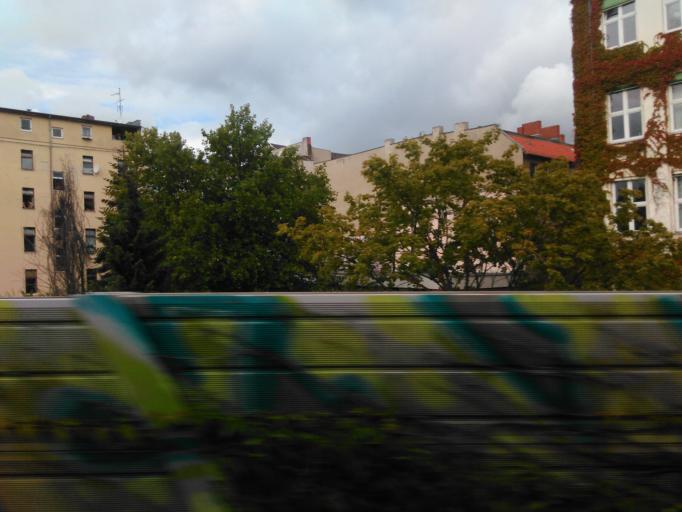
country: DE
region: Berlin
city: Wedding Bezirk
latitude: 52.5450
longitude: 13.3717
